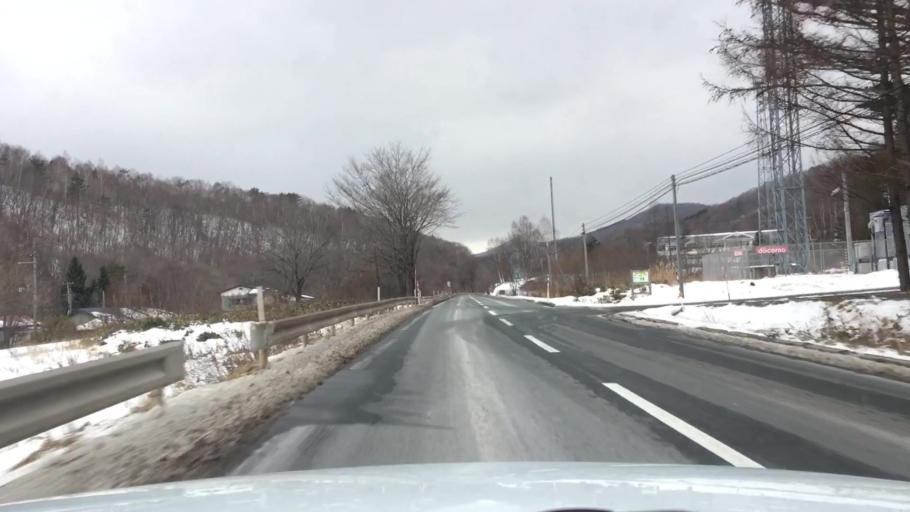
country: JP
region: Iwate
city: Morioka-shi
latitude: 39.6382
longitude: 141.4283
